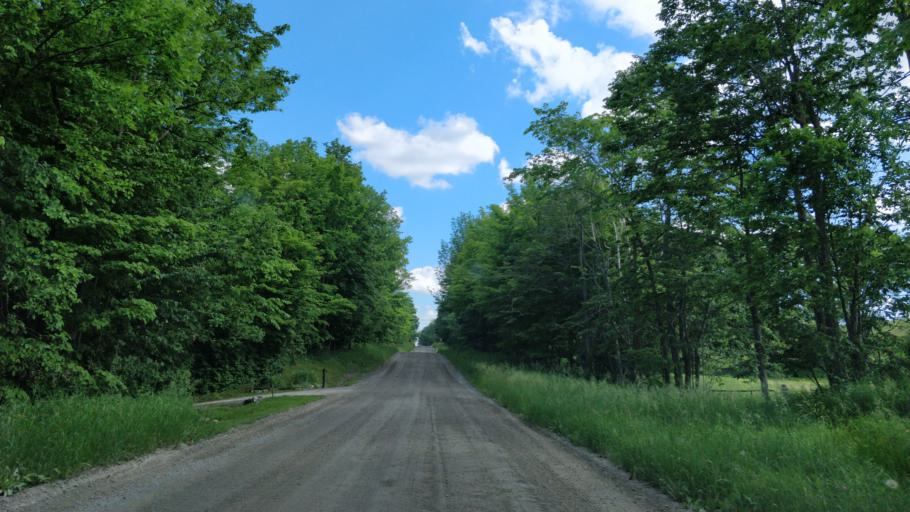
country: CA
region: Ontario
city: Perth
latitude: 44.6612
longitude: -76.5428
